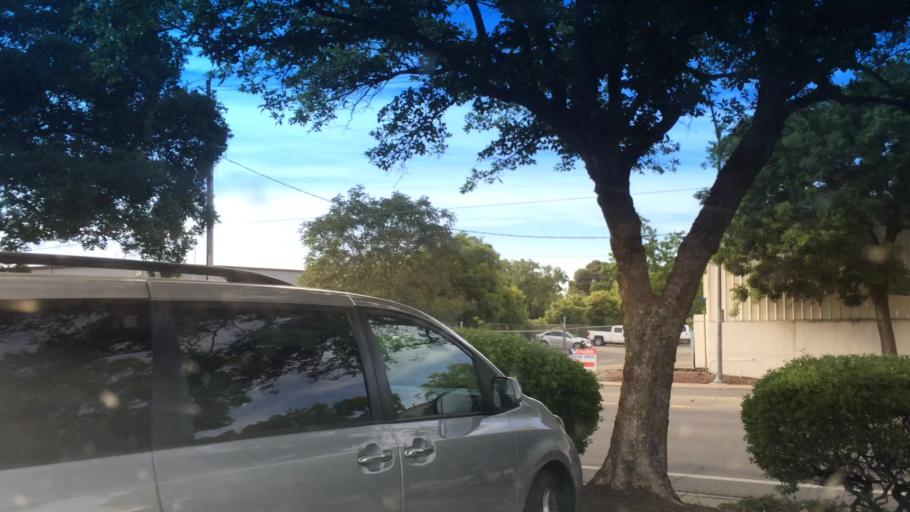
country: US
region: California
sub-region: Butte County
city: Chico
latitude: 39.7248
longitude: -121.8152
